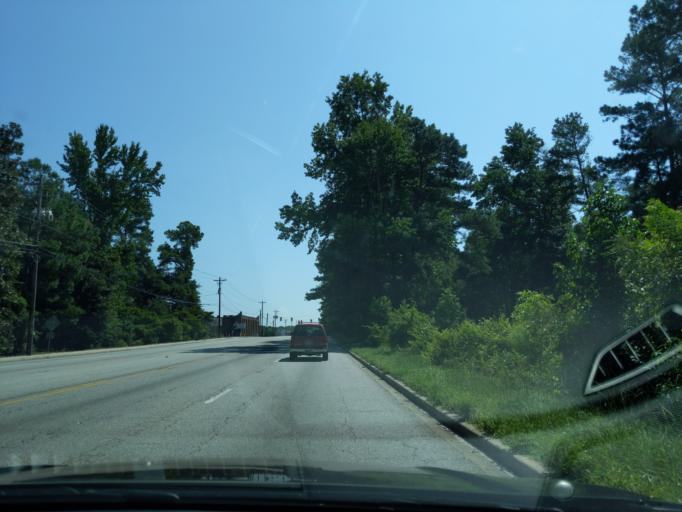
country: US
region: South Carolina
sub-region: Lexington County
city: Oak Grove
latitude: 33.9725
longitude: -81.1365
